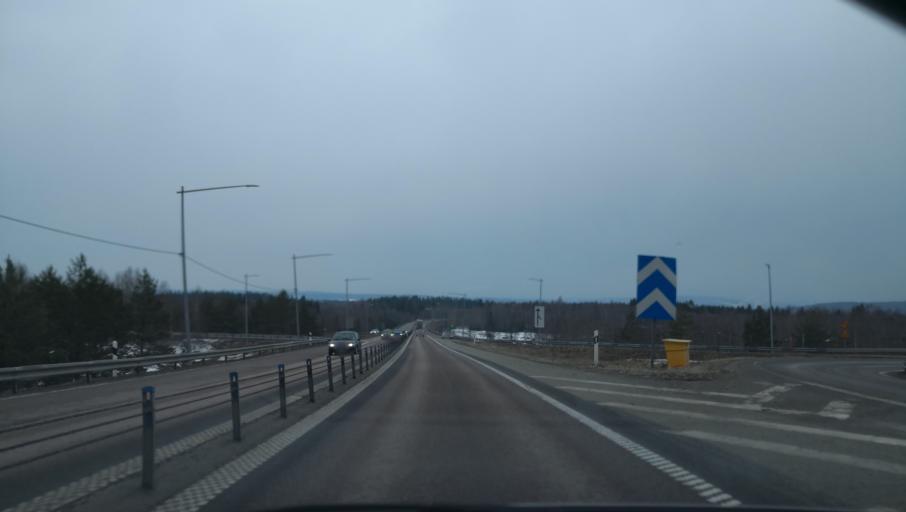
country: SE
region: Vaesternorrland
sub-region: Timra Kommun
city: Soraker
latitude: 62.5264
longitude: 17.4753
